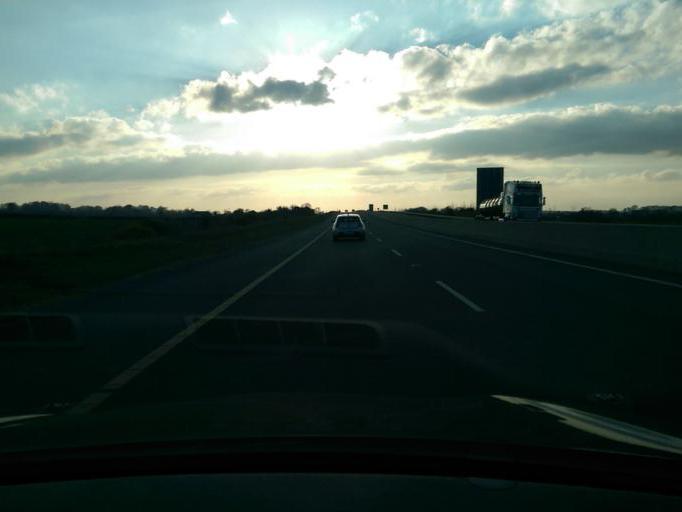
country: IE
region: Munster
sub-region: North Tipperary
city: Templemore
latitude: 52.8853
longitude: -7.9541
